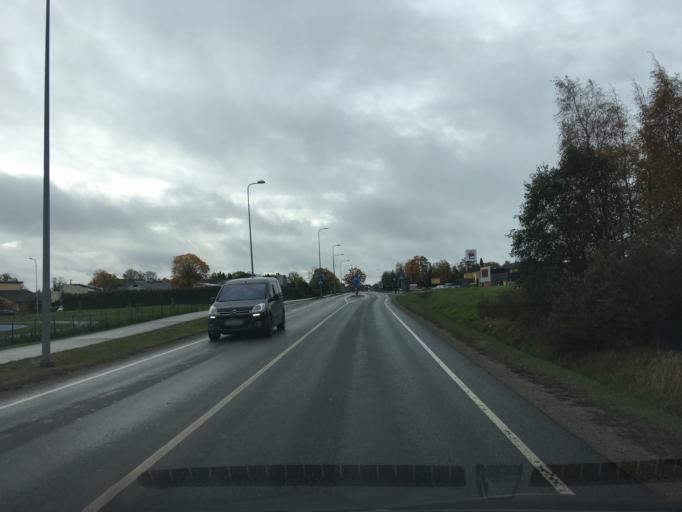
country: EE
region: Harju
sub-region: Saku vald
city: Saku
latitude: 59.2955
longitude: 24.6553
